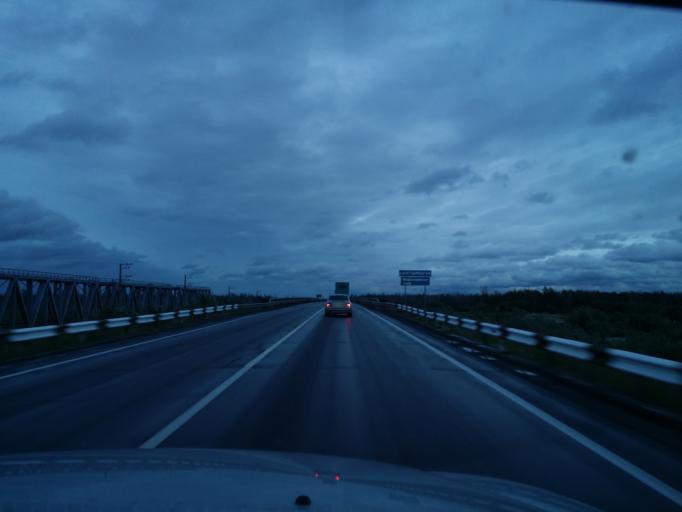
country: RU
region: Khanty-Mansiyskiy Avtonomnyy Okrug
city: Lokosovo
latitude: 61.4563
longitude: 74.6696
